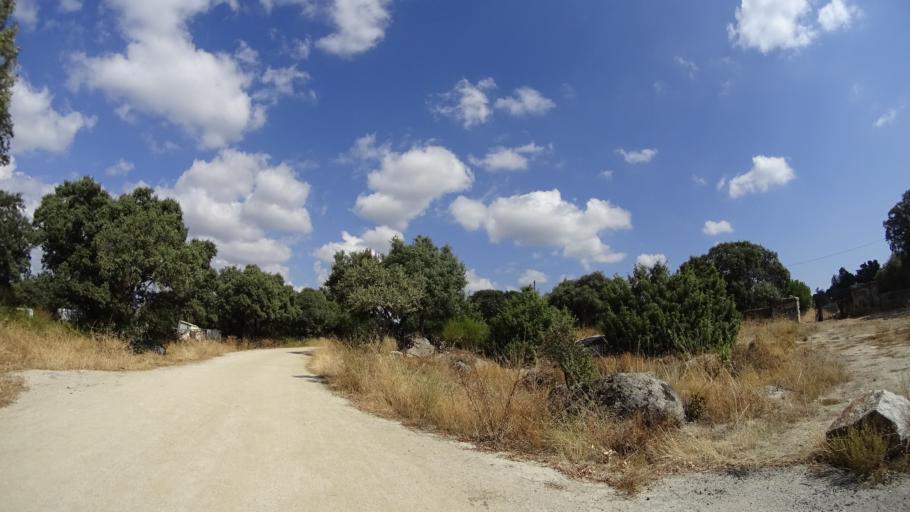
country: ES
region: Madrid
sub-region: Provincia de Madrid
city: Galapagar
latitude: 40.5893
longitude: -3.9962
